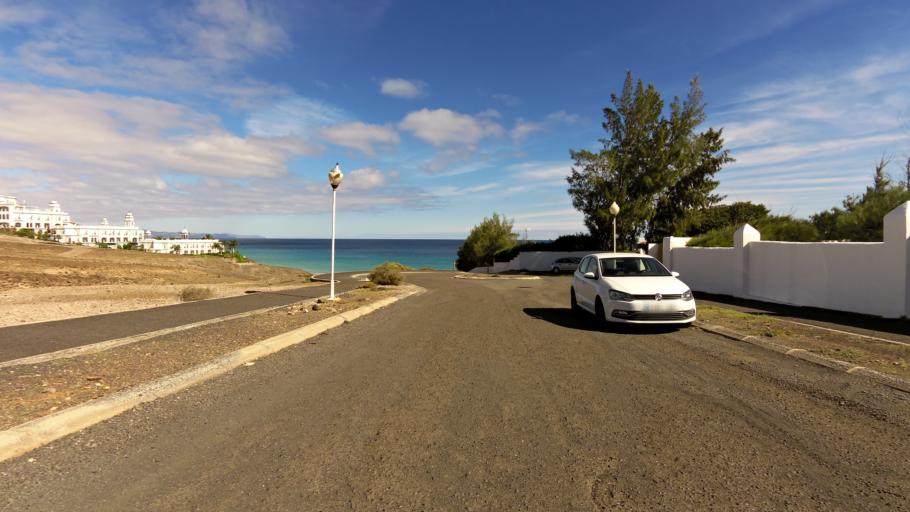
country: ES
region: Canary Islands
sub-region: Provincia de Las Palmas
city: Pajara
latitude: 28.0609
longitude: -14.3145
